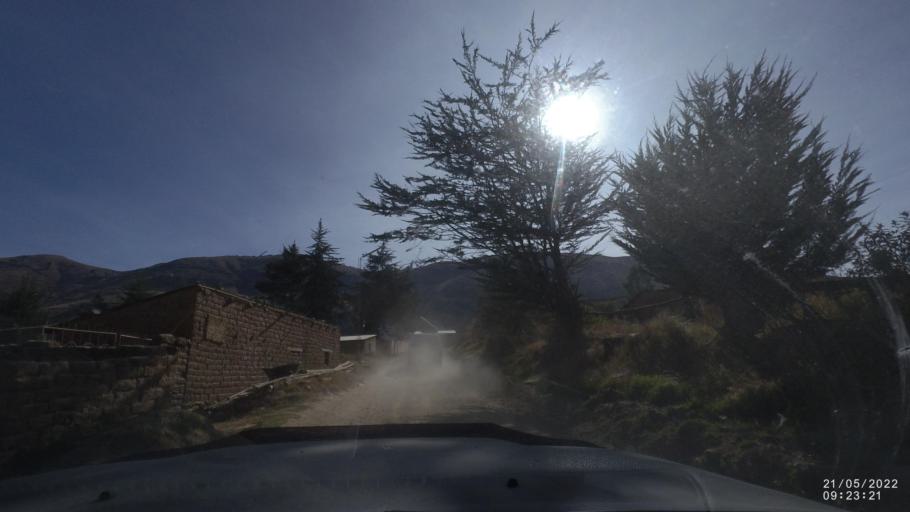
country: BO
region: Cochabamba
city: Colomi
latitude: -17.3448
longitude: -66.0125
